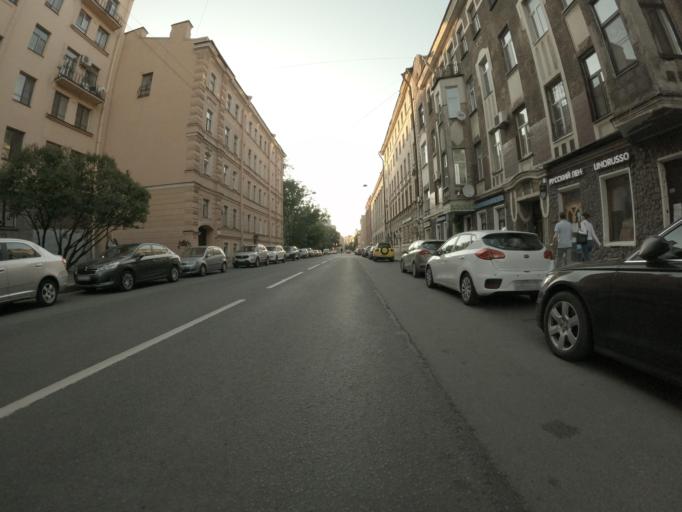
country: RU
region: St.-Petersburg
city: Petrogradka
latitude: 59.9573
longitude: 30.3134
